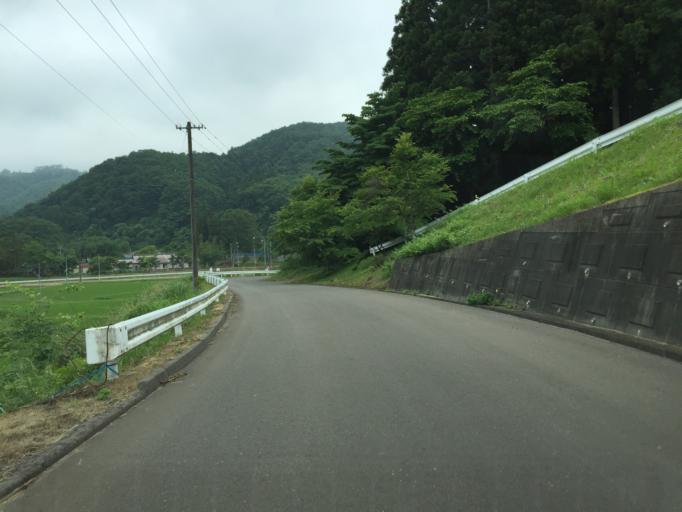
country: JP
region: Miyagi
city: Marumori
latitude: 37.7983
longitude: 140.7447
